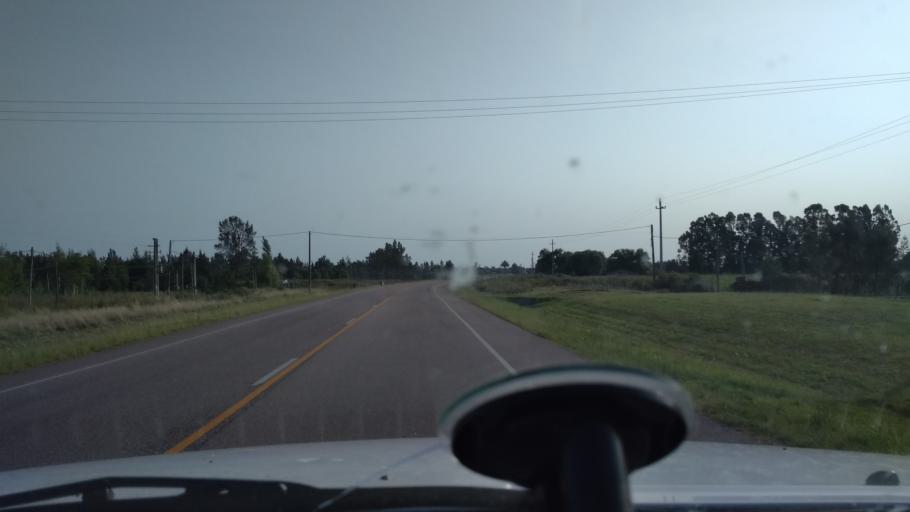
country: UY
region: Canelones
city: Sauce
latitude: -34.6517
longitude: -56.0515
